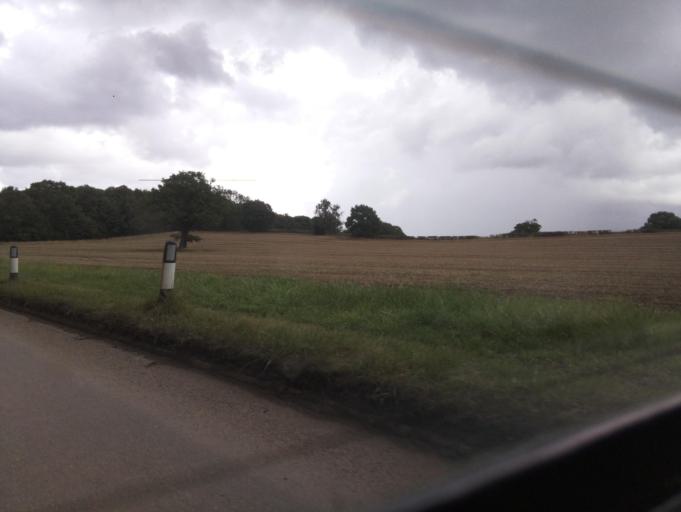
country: GB
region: England
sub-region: Staffordshire
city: Eccleshall
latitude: 52.8980
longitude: -2.2148
